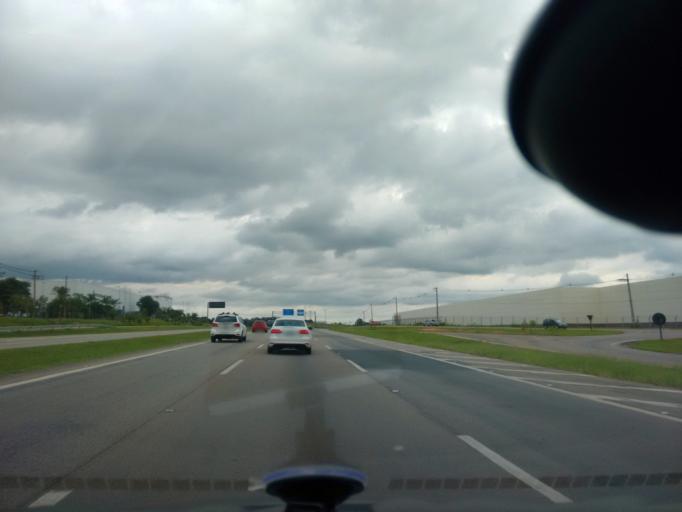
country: BR
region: Sao Paulo
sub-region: Indaiatuba
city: Indaiatuba
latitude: -23.0789
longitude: -47.1707
